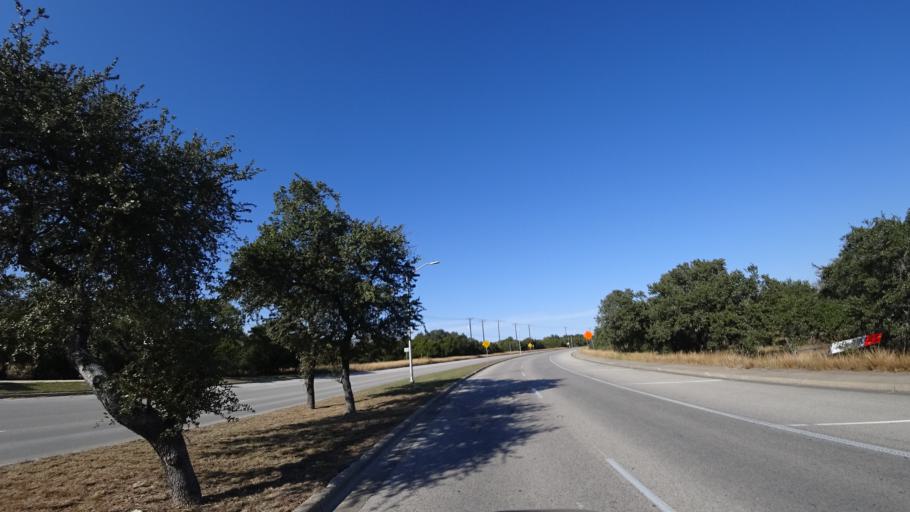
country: US
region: Texas
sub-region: Williamson County
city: Cedar Park
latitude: 30.4907
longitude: -97.8605
